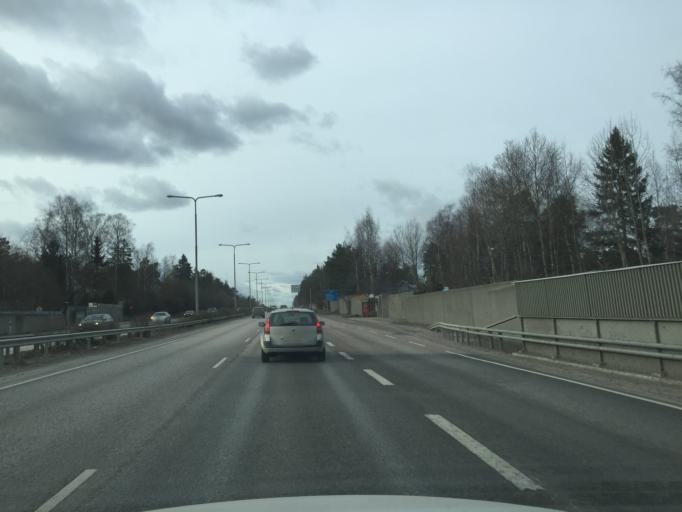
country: FI
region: Uusimaa
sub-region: Helsinki
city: Teekkarikylae
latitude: 60.2407
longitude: 24.8951
